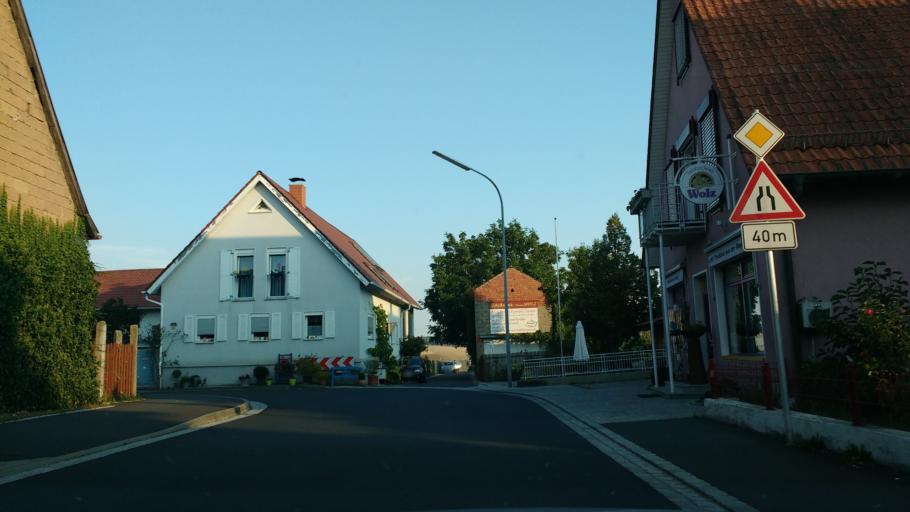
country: DE
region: Bavaria
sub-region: Regierungsbezirk Unterfranken
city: Wasserlosen
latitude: 50.0761
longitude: 10.0387
